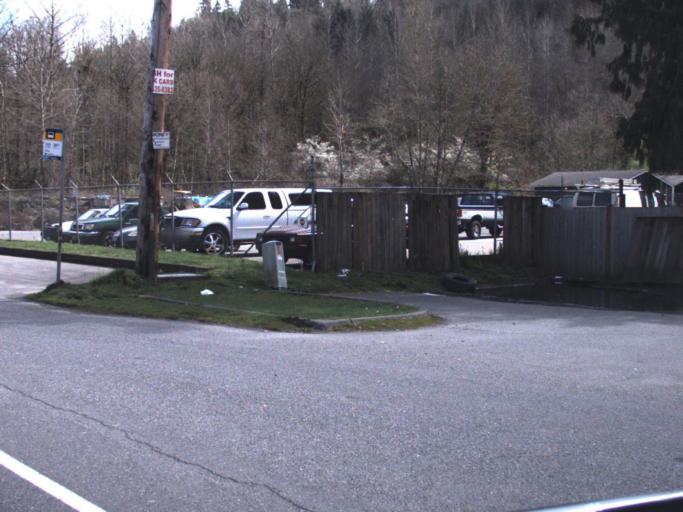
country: US
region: Washington
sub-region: King County
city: Maple Heights-Lake Desire
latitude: 47.4627
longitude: -122.1010
